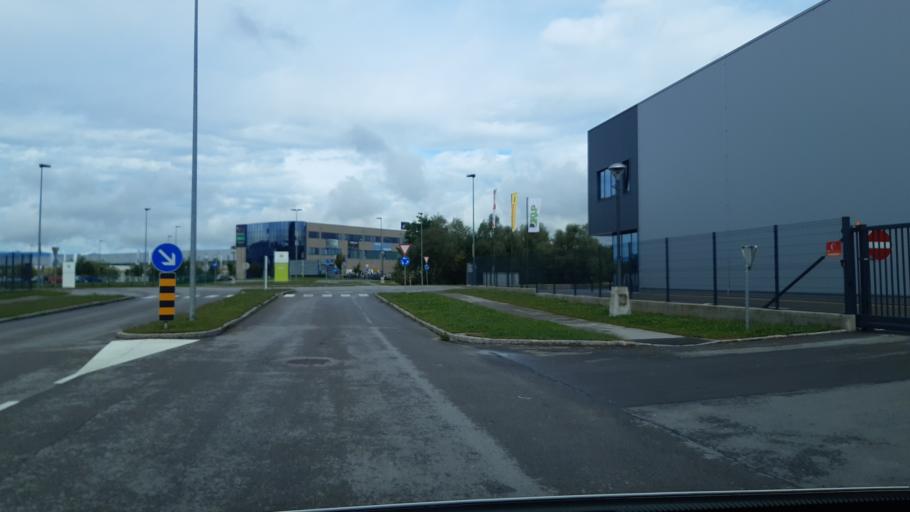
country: SI
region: Komenda
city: Komenda
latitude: 46.1889
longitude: 14.5217
